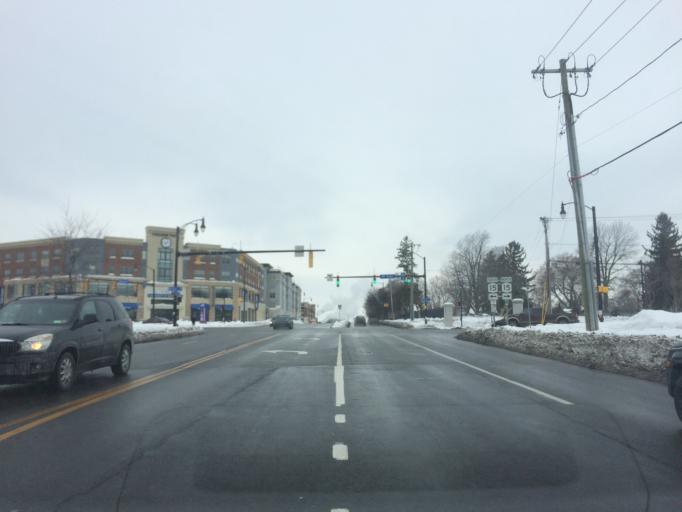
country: US
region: New York
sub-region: Monroe County
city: Rochester
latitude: 43.1248
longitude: -77.6167
